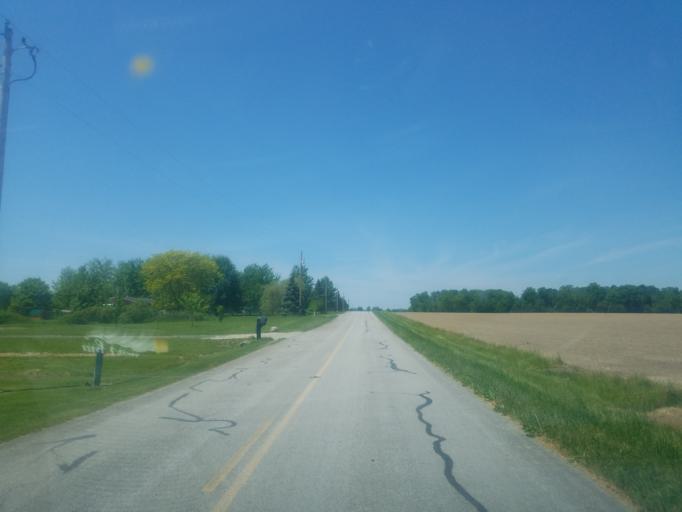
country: US
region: Ohio
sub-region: Huron County
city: New London
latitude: 41.1161
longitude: -82.3847
